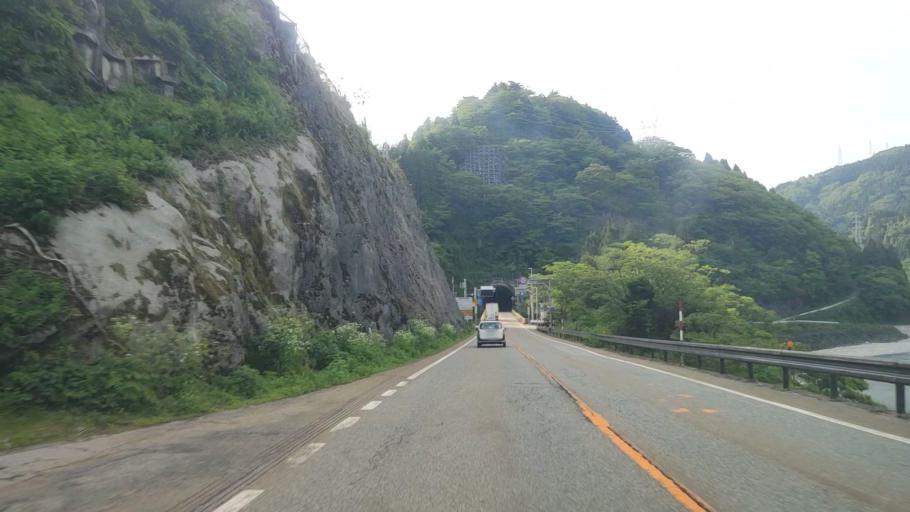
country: JP
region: Toyama
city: Yatsuomachi-higashikumisaka
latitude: 36.4602
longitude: 137.2482
